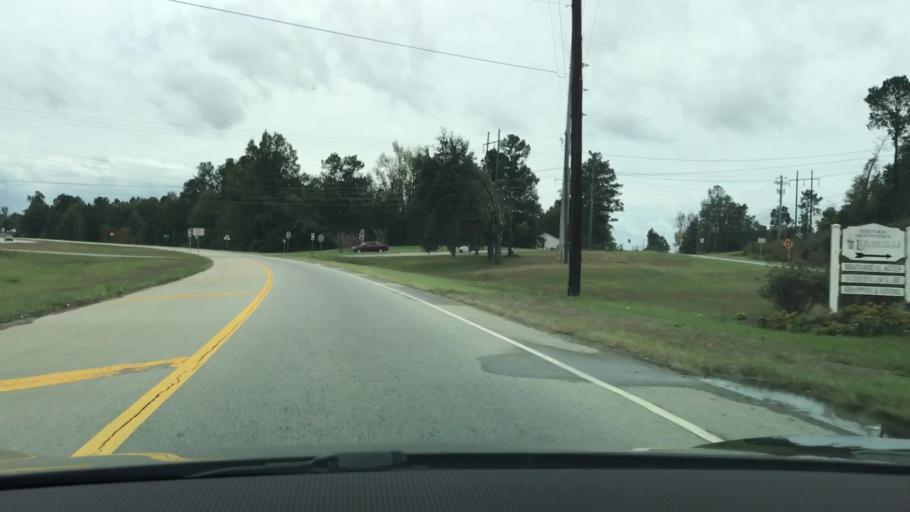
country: US
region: Georgia
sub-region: Jefferson County
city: Louisville
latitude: 33.0161
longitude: -82.4040
